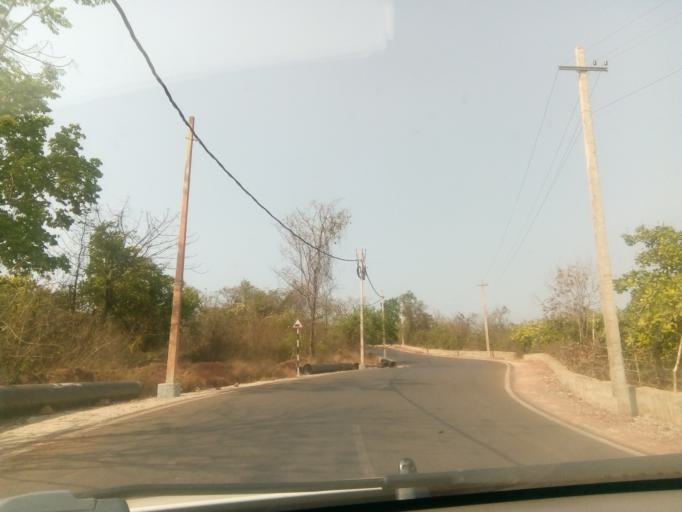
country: IN
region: Goa
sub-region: North Goa
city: Pernem
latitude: 15.7228
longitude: 73.8543
